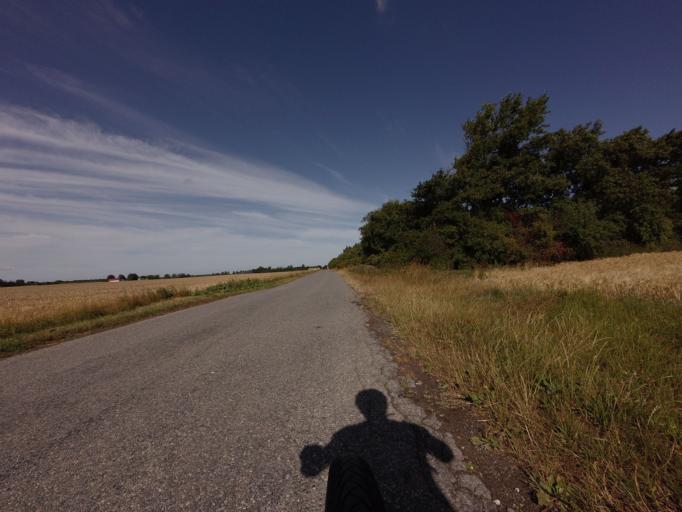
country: DK
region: North Denmark
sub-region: Hjorring Kommune
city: Vra
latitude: 57.3912
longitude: 9.9739
